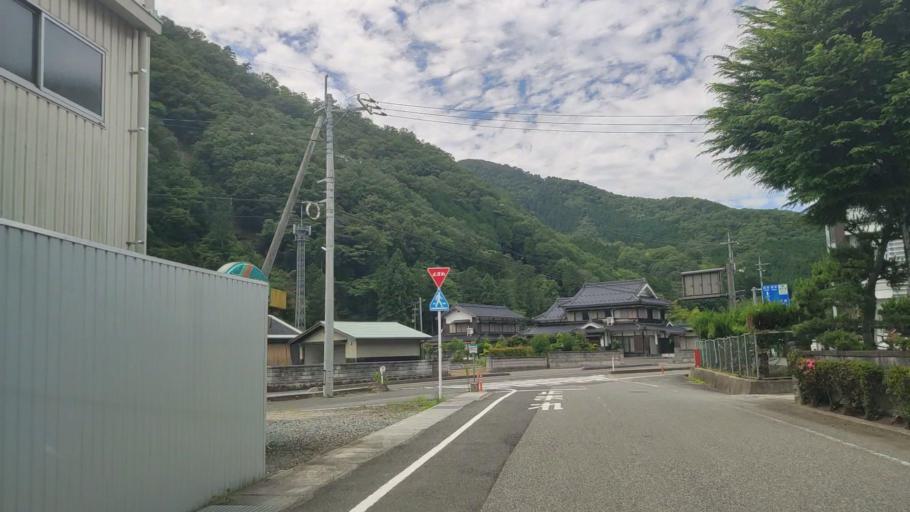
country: JP
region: Hyogo
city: Yamazakicho-nakabirose
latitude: 35.1094
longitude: 134.3271
